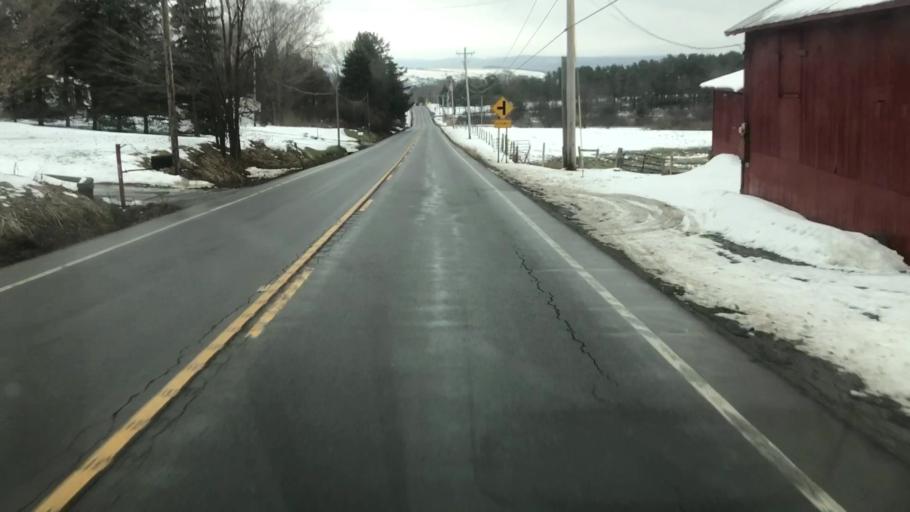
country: US
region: New York
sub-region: Cortland County
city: Homer
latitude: 42.6385
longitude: -76.2128
